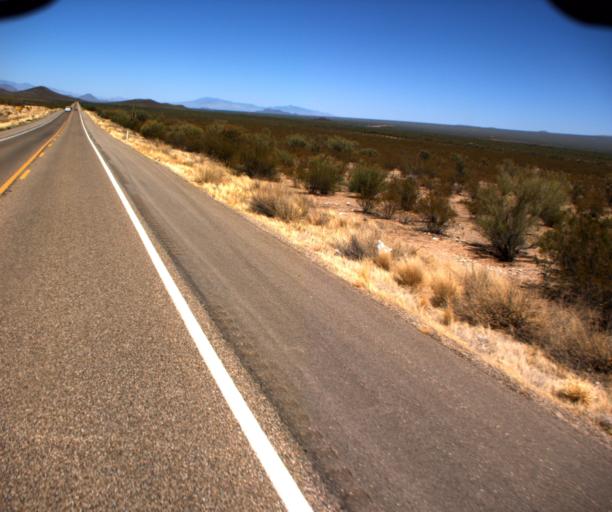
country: US
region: Arizona
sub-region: Pima County
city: Three Points
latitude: 32.0444
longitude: -111.4358
